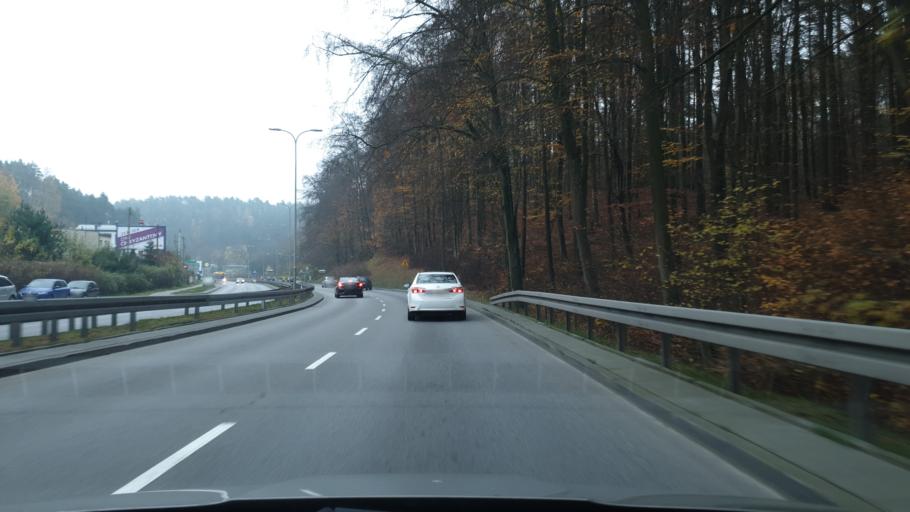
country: PL
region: Pomeranian Voivodeship
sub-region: Powiat gdanski
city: Kowale
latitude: 54.3717
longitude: 18.5537
